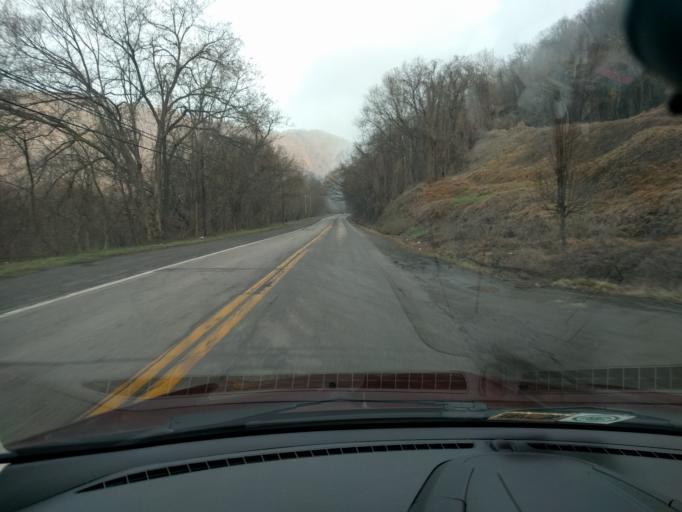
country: US
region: West Virginia
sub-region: Kanawha County
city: Montgomery
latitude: 38.1583
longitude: -81.2958
